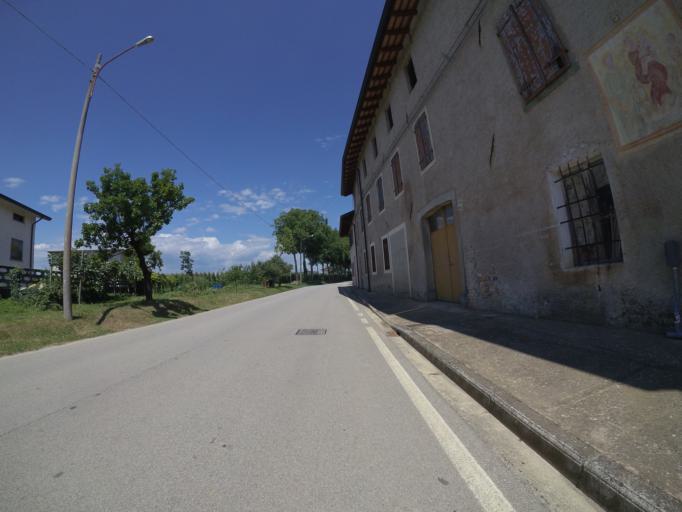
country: IT
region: Friuli Venezia Giulia
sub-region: Provincia di Udine
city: Bertiolo
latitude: 45.9402
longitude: 13.0725
